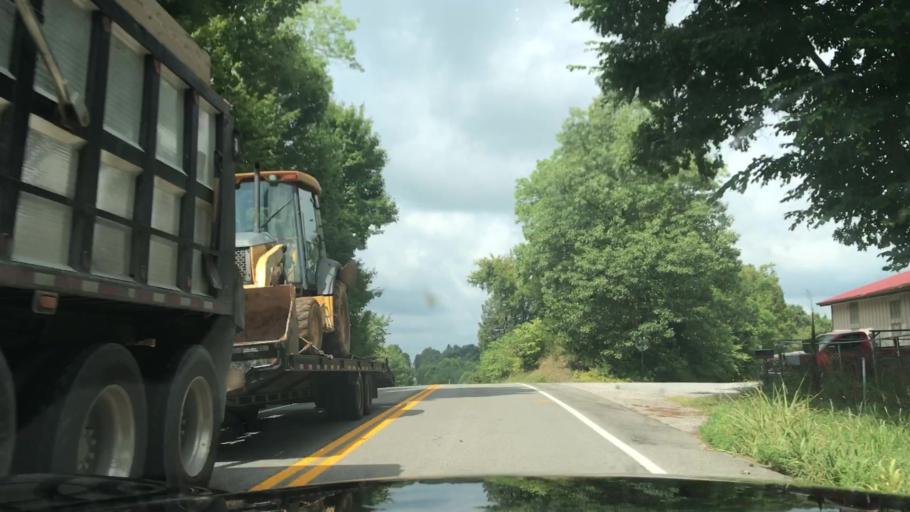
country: US
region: Kentucky
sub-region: Muhlenberg County
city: Central City
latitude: 37.2044
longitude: -86.9527
